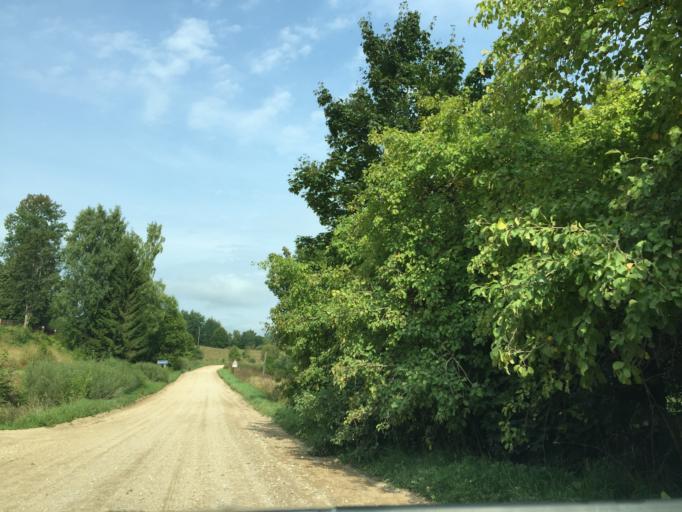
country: LV
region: Ludzas Rajons
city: Ludza
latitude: 56.3207
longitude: 27.7665
